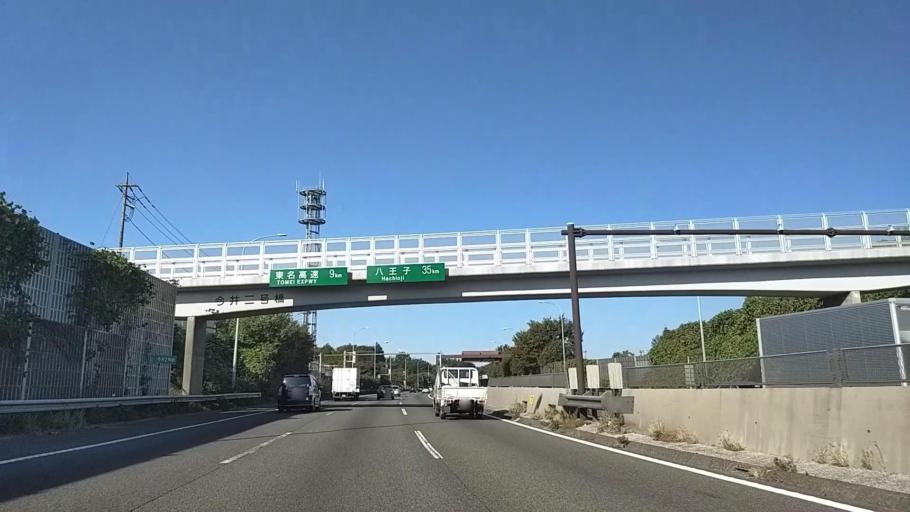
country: JP
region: Kanagawa
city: Yokohama
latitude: 35.4537
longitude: 139.5560
